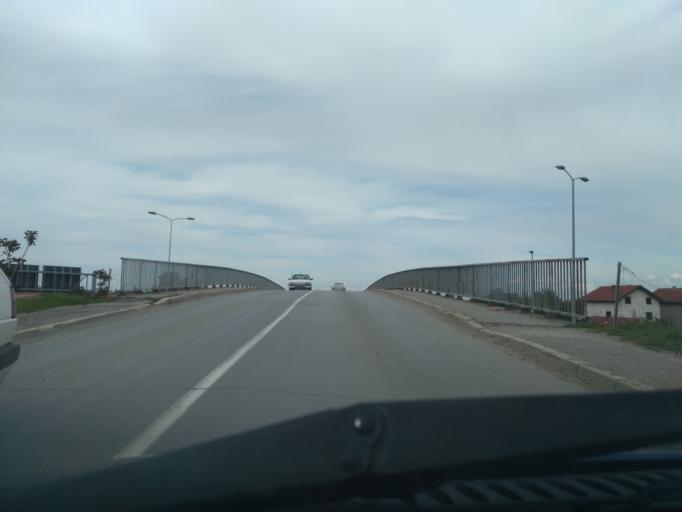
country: RS
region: Central Serbia
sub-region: Podunavski Okrug
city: Velika Plana
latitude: 44.3420
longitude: 21.0809
